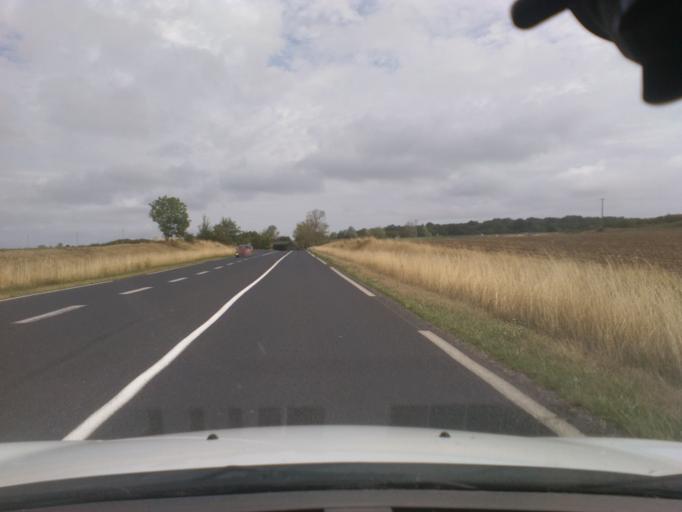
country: FR
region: Lorraine
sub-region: Departement de Meurthe-et-Moselle
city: Flavigny-sur-Moselle
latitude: 48.5492
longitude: 6.1889
